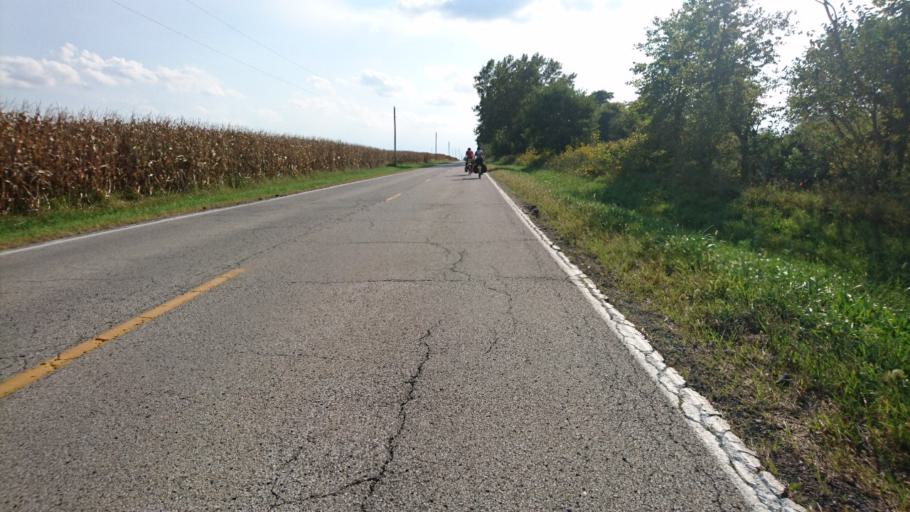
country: US
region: Illinois
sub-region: Logan County
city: Atlanta
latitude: 40.3088
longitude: -89.1762
